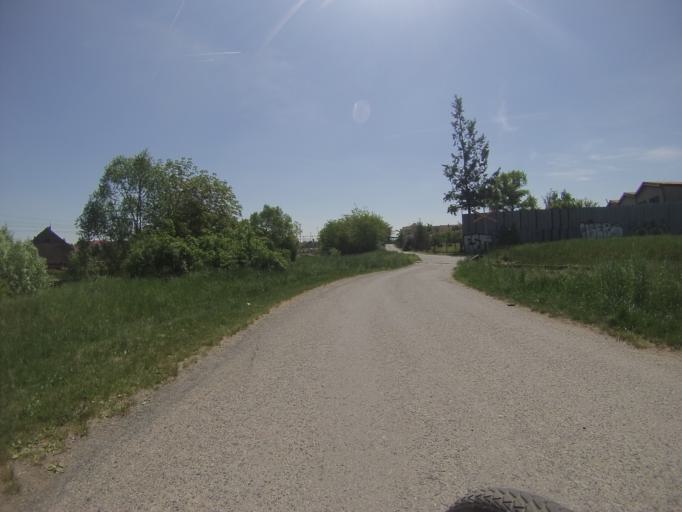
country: CZ
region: South Moravian
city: Vranovice
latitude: 48.9685
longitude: 16.6016
